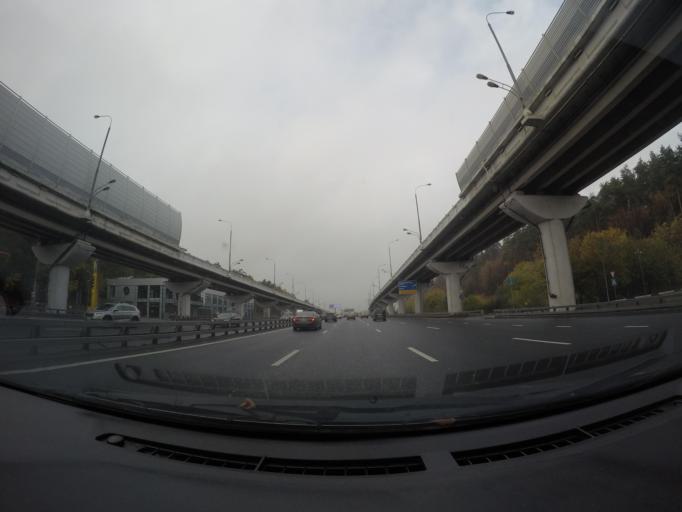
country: RU
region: Moscow
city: Rublevo
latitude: 55.7913
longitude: 37.3651
